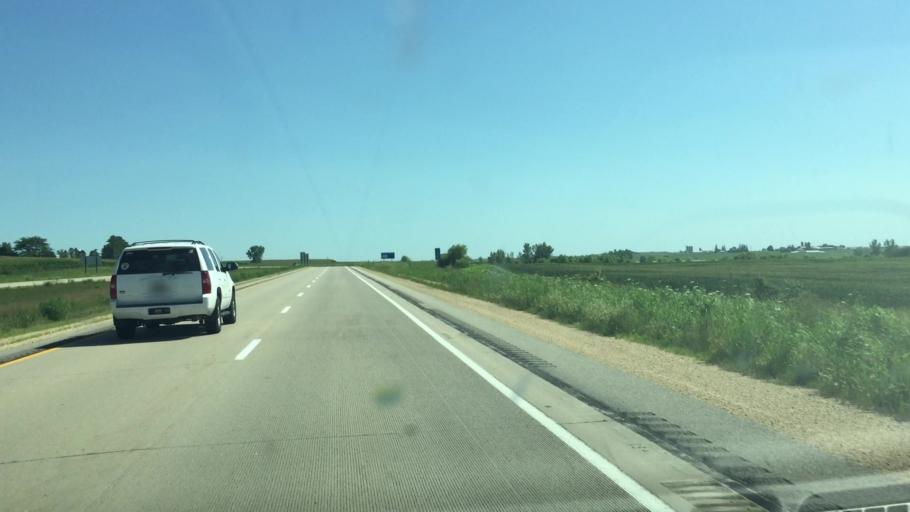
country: US
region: Iowa
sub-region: Jones County
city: Monticello
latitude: 42.2151
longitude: -91.1738
